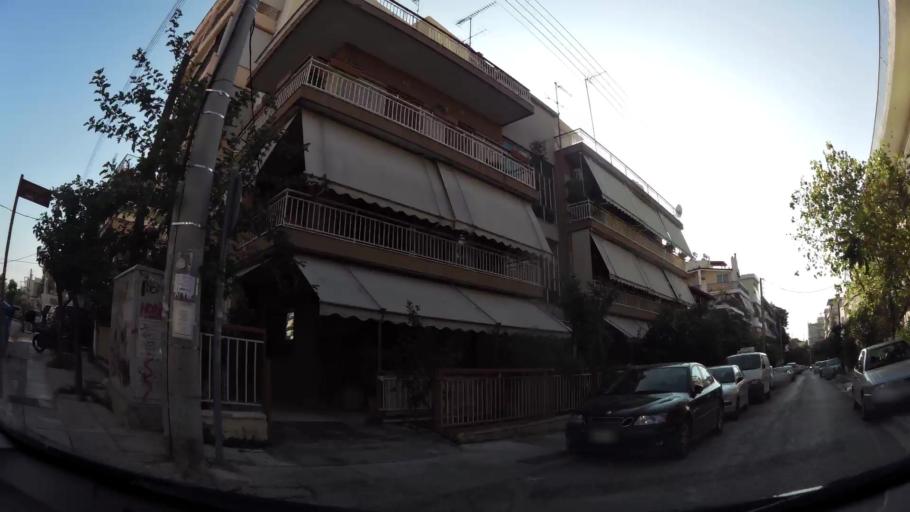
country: GR
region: Attica
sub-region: Nomarchia Athinas
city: Argyroupoli
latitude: 37.8929
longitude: 23.7534
